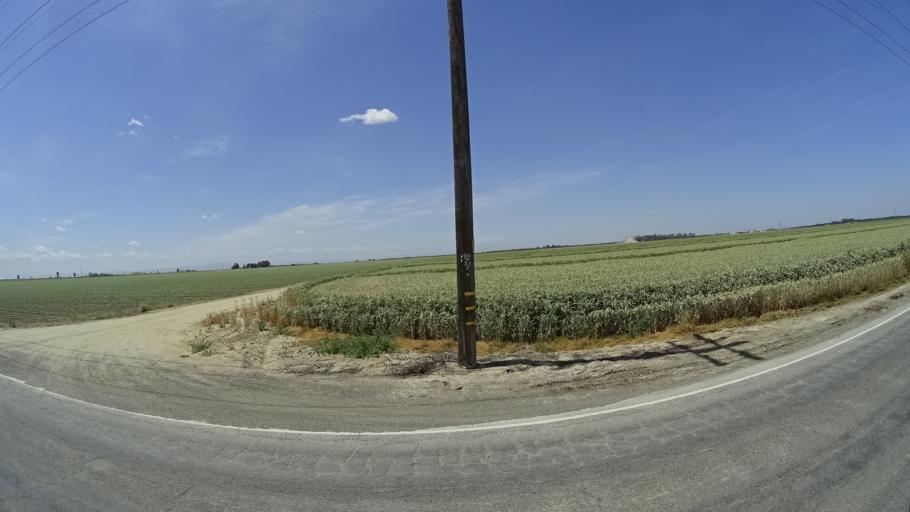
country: US
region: California
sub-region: Kings County
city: Home Garden
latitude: 36.2439
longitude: -119.6549
